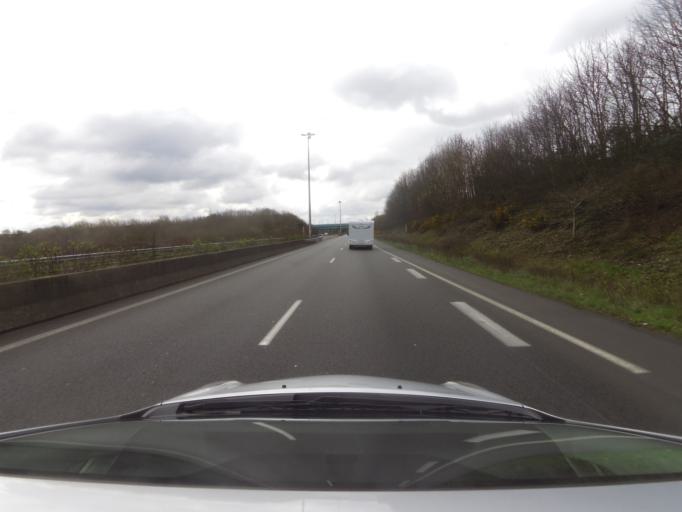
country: FR
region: Nord-Pas-de-Calais
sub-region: Departement du Pas-de-Calais
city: Saint-Martin-Boulogne
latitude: 50.7433
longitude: 1.6283
